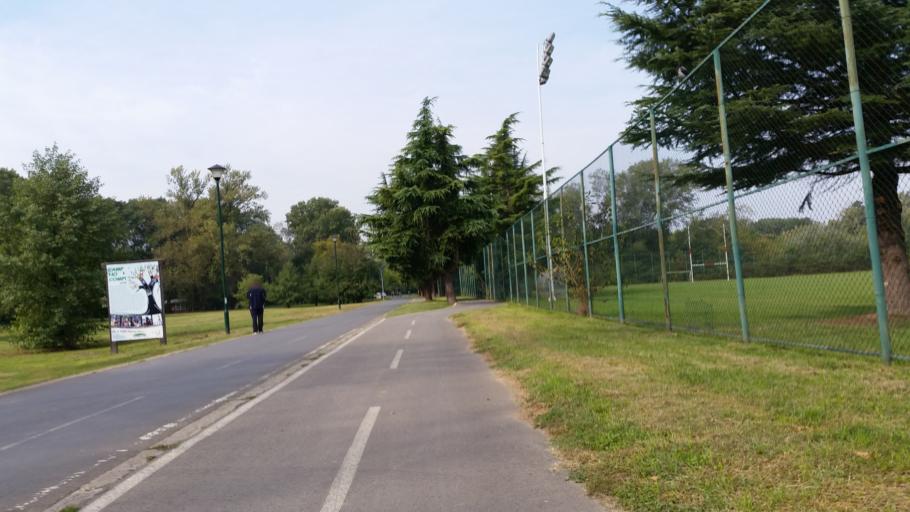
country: RS
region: Central Serbia
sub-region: Belgrade
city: Cukarica
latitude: 44.7883
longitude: 20.3978
